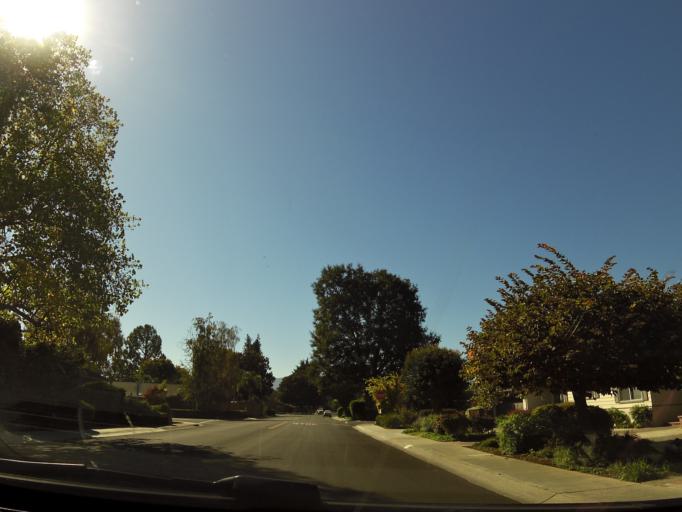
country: US
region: California
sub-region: Santa Clara County
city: Campbell
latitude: 37.2855
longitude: -121.9271
